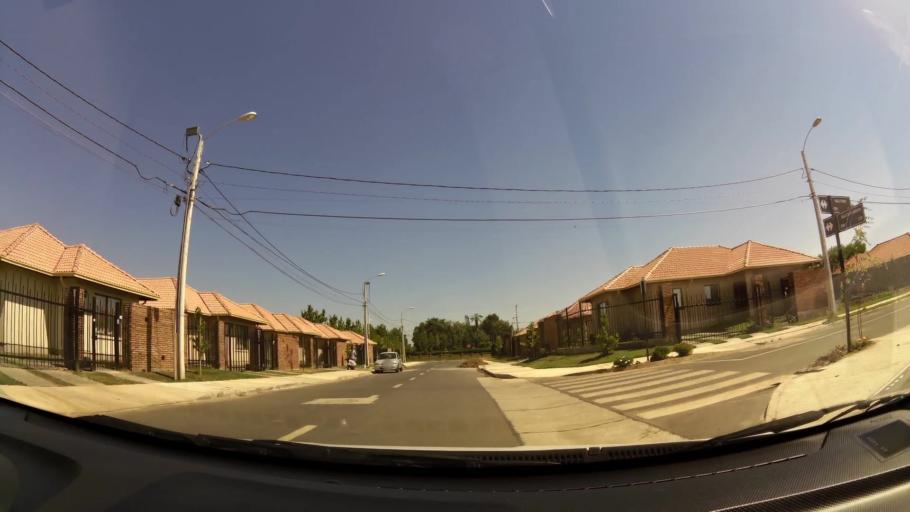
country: CL
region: Maule
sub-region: Provincia de Talca
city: Talca
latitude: -35.4338
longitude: -71.5945
